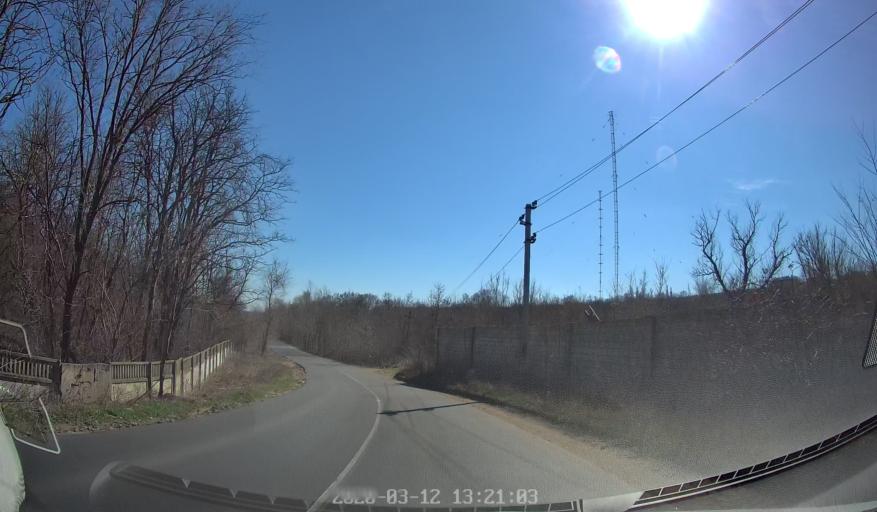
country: MD
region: Laloveni
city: Ialoveni
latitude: 46.9556
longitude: 28.8302
